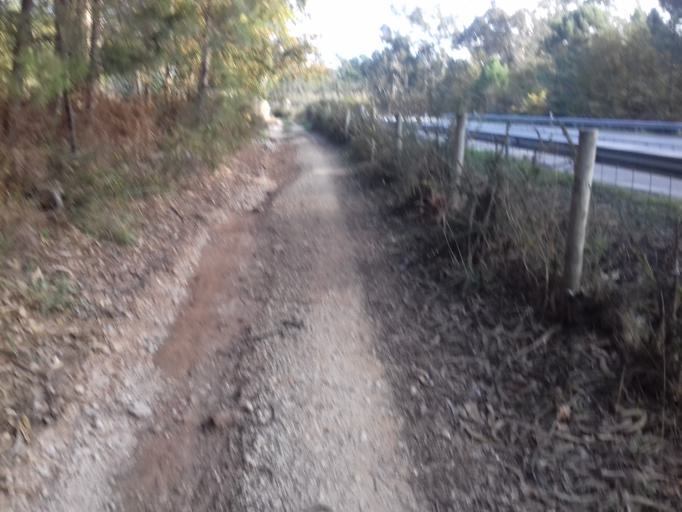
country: PT
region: Aveiro
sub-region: Estarreja
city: Beduido
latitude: 40.7894
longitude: -8.5406
